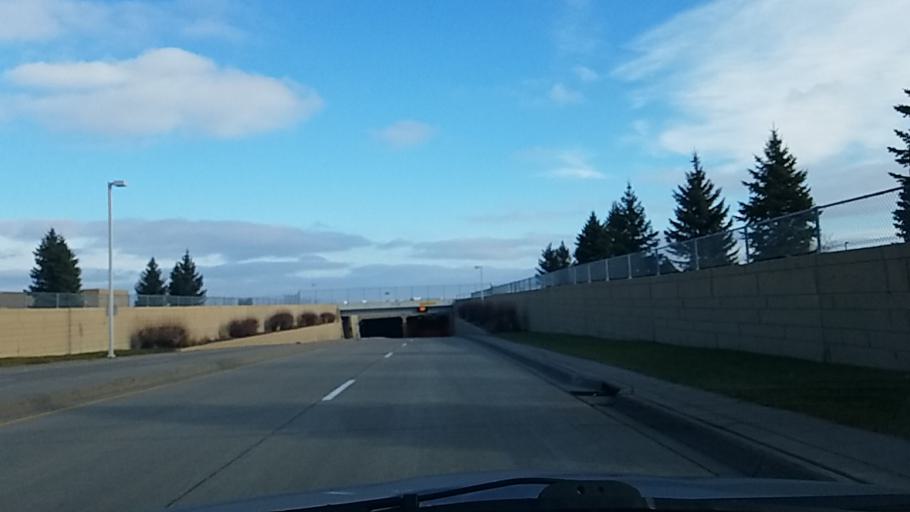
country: US
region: Minnesota
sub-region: Hennepin County
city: Richfield
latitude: 44.8759
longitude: -93.2433
